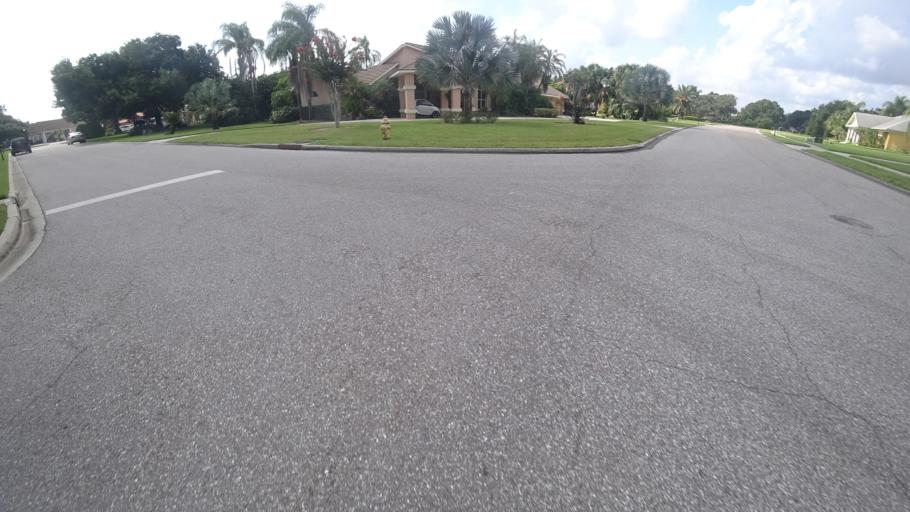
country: US
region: Florida
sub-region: Sarasota County
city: The Meadows
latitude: 27.4329
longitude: -82.4396
